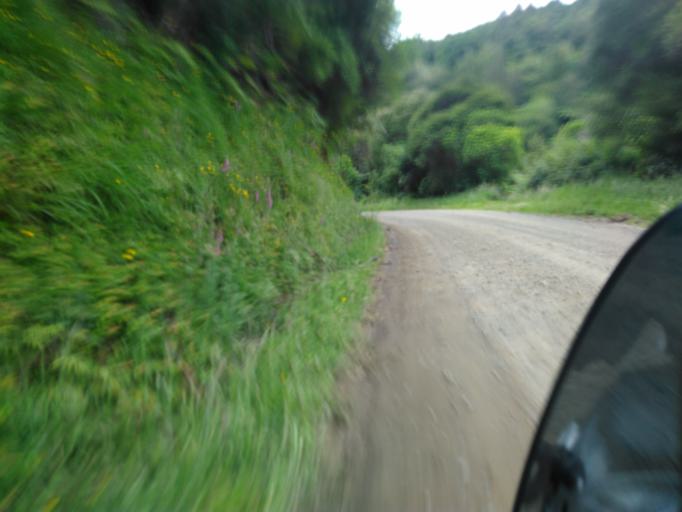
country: NZ
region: Bay of Plenty
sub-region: Opotiki District
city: Opotiki
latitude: -38.0343
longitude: 177.4433
